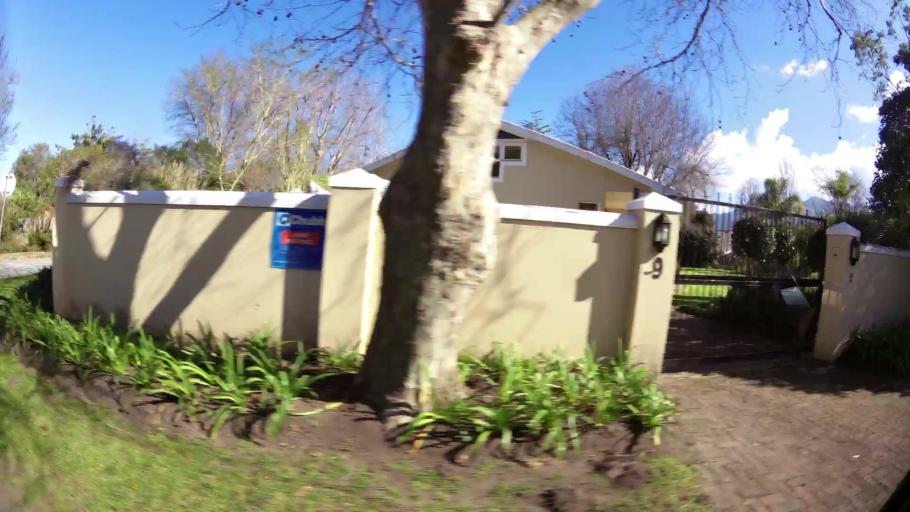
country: ZA
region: Western Cape
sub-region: Eden District Municipality
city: George
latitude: -33.9499
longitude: 22.4408
